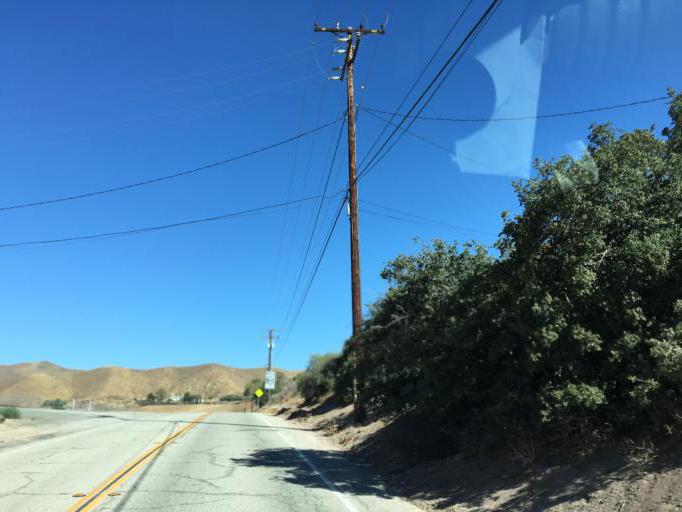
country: US
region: California
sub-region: Los Angeles County
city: Agua Dulce
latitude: 34.4815
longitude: -118.3713
